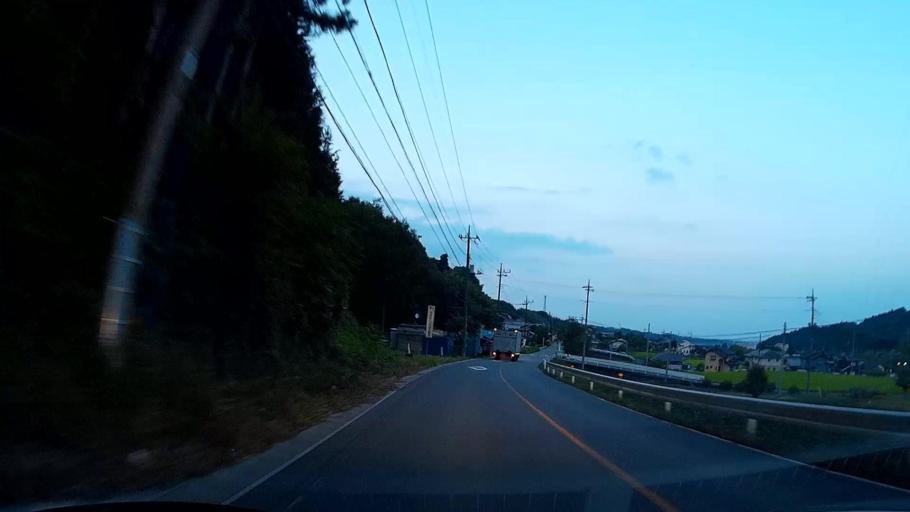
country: JP
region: Gunma
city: Annaka
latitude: 36.3839
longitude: 138.8679
